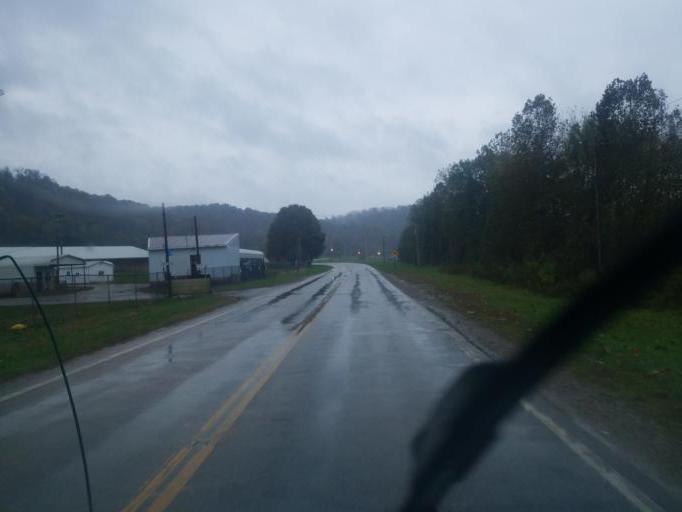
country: US
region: Ohio
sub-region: Morgan County
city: McConnelsville
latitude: 39.6398
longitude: -81.8404
